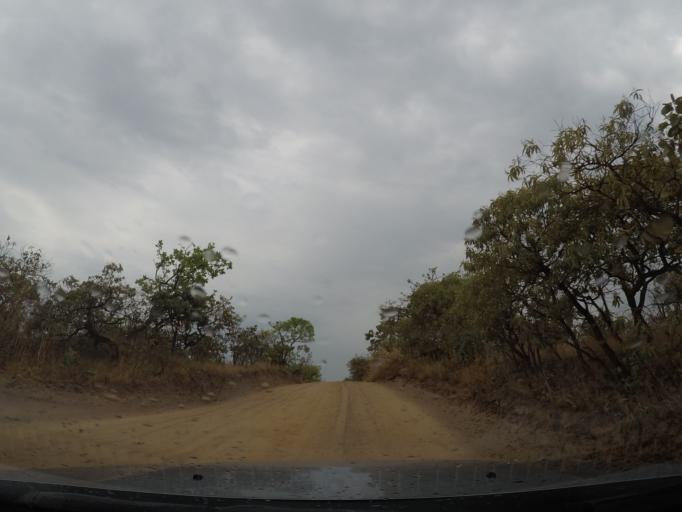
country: BR
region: Goias
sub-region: Pirenopolis
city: Pirenopolis
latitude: -15.8390
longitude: -48.9131
